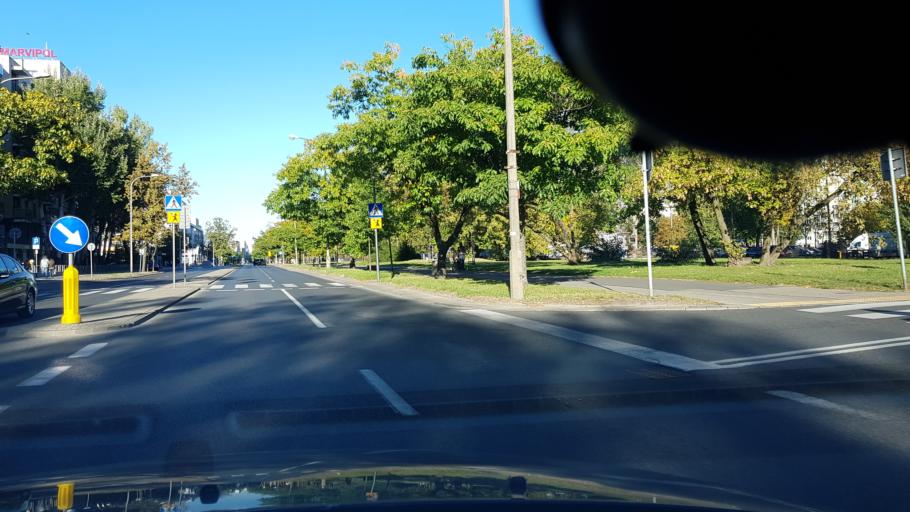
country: PL
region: Masovian Voivodeship
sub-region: Warszawa
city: Bielany
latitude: 52.2827
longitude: 20.9262
